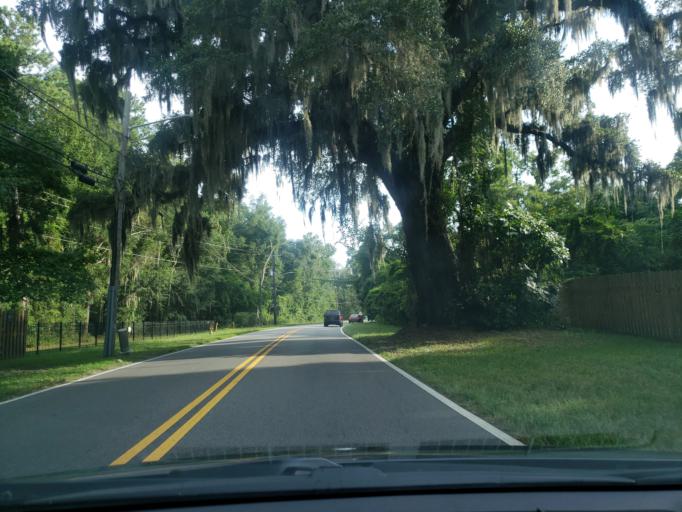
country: US
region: Georgia
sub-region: Chatham County
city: Montgomery
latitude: 31.9616
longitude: -81.1363
